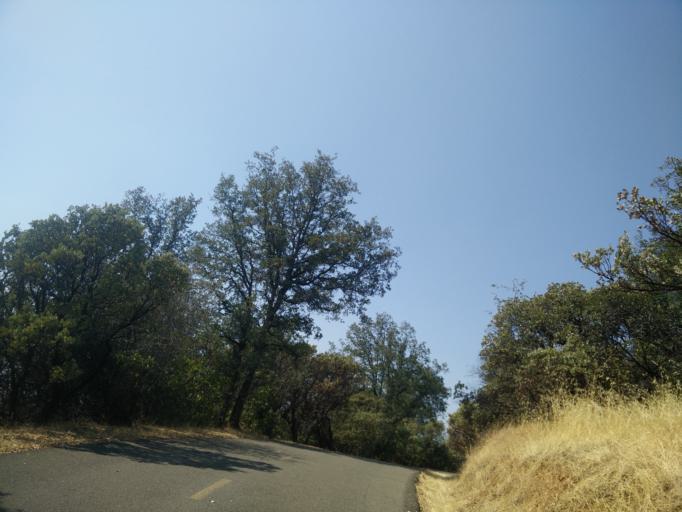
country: US
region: California
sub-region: Shasta County
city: Redding
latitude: 40.5953
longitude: -122.4288
